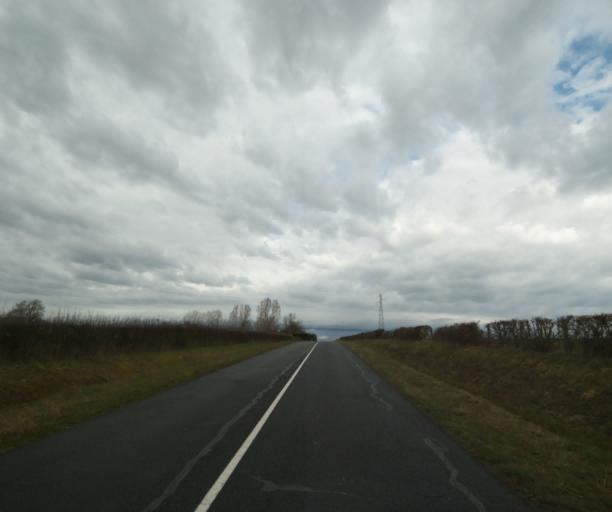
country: FR
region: Auvergne
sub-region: Departement de l'Allier
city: Toulon-sur-Allier
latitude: 46.5026
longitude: 3.3769
